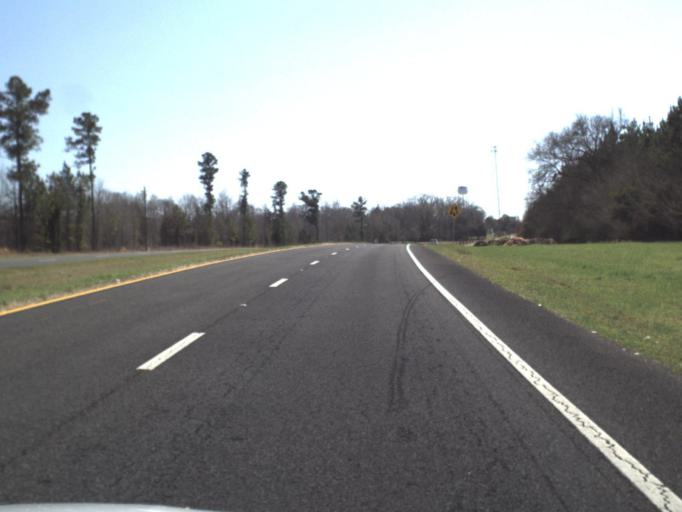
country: US
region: Florida
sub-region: Jackson County
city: Graceville
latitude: 30.9584
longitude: -85.4031
